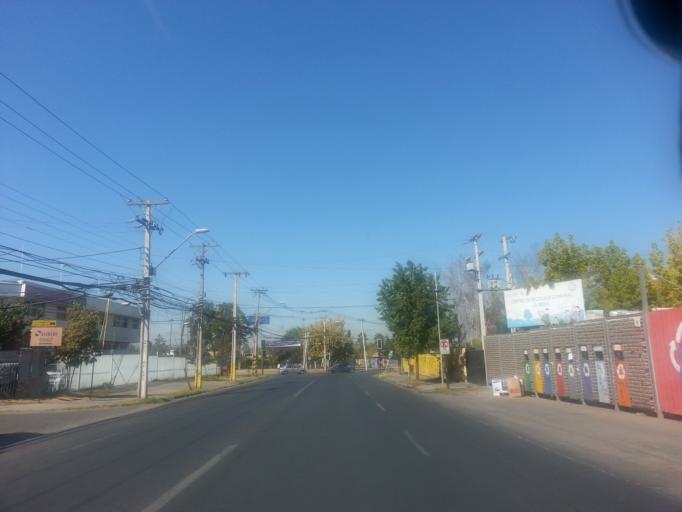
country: CL
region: Santiago Metropolitan
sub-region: Provincia de Santiago
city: Villa Presidente Frei, Nunoa, Santiago, Chile
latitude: -33.4575
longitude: -70.5454
